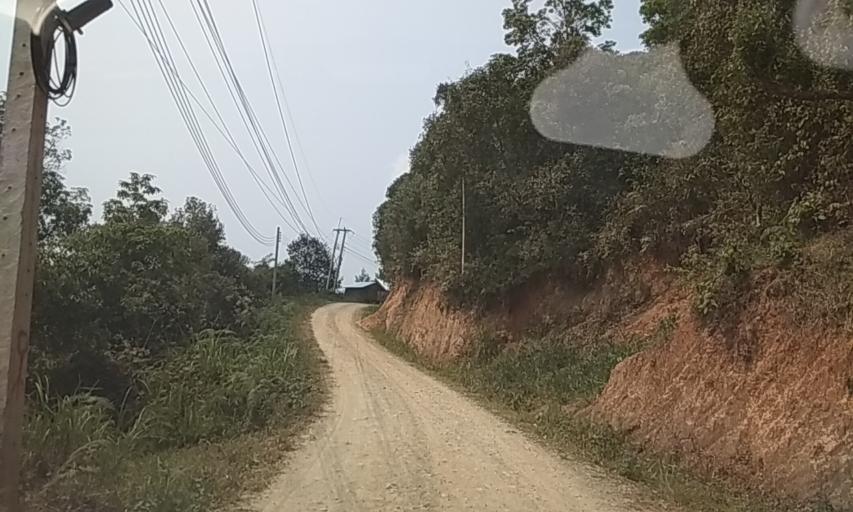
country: TH
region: Nan
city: Chaloem Phra Kiat
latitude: 20.0502
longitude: 101.0636
